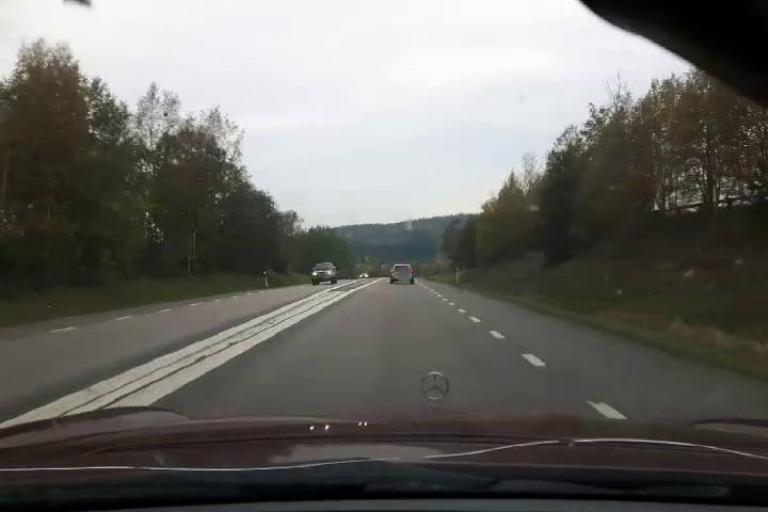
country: SE
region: Vaesternorrland
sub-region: Kramfors Kommun
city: Nordingra
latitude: 63.0270
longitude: 18.3009
